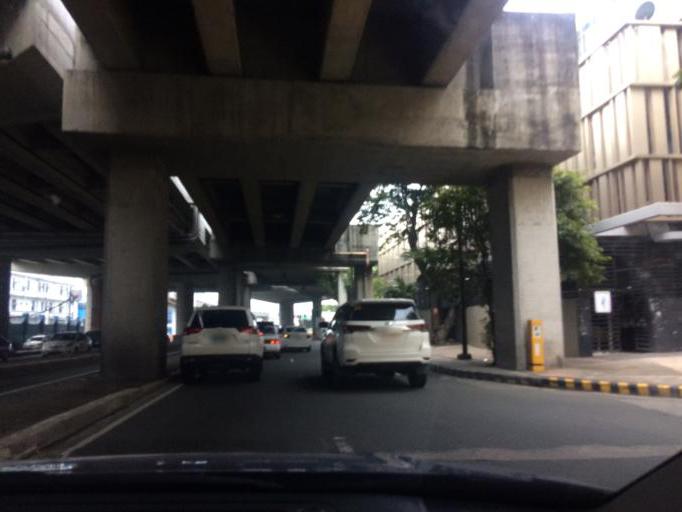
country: PH
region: Metro Manila
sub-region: Makati City
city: Makati City
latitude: 14.5182
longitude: 121.0201
